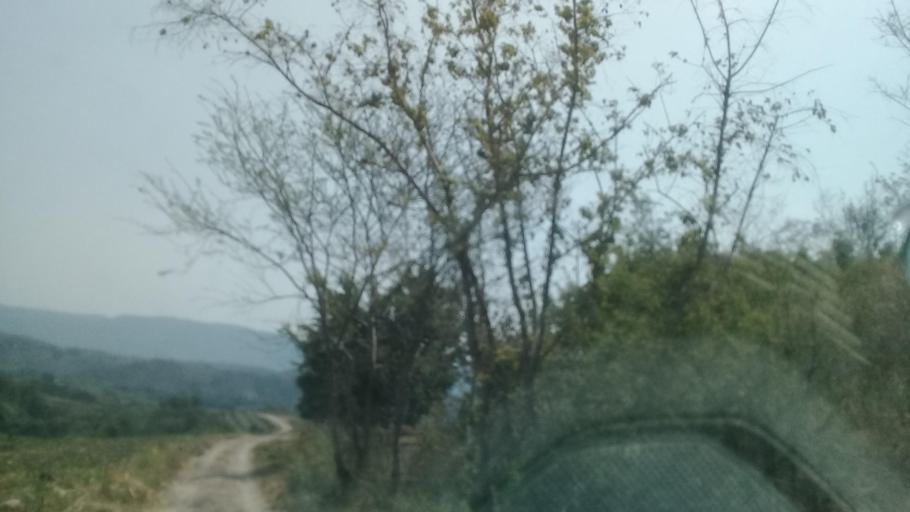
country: MX
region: Veracruz
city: El Castillo
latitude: 19.5710
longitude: -96.8049
